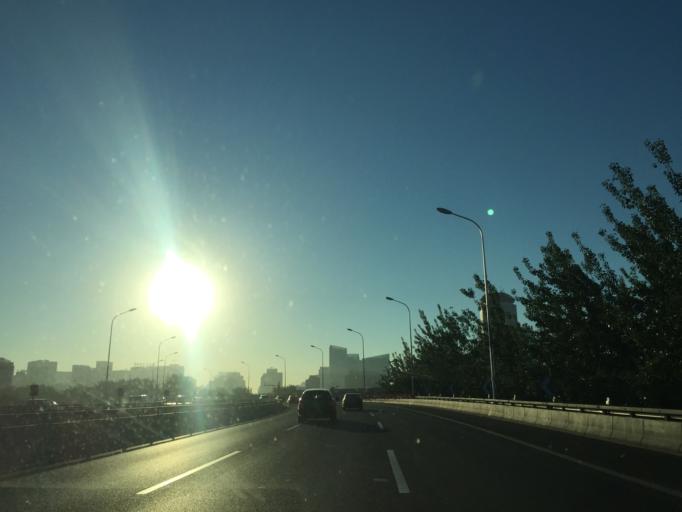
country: CN
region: Beijing
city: Chaowai
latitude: 39.9481
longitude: 116.4371
